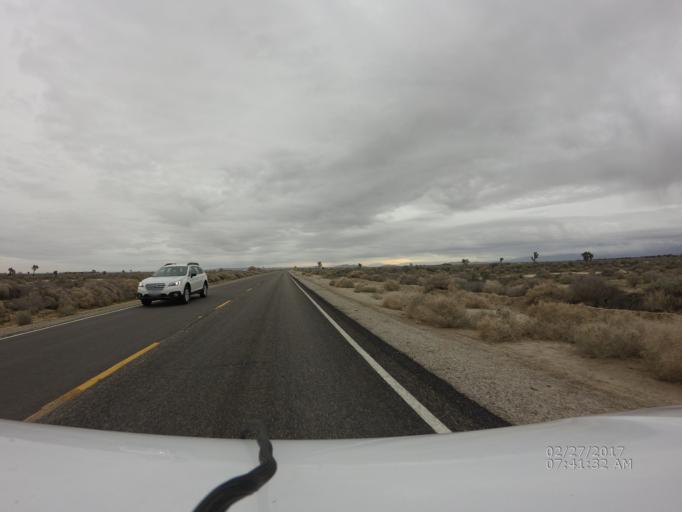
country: US
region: California
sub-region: Los Angeles County
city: Lancaster
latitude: 34.7193
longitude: -118.0624
